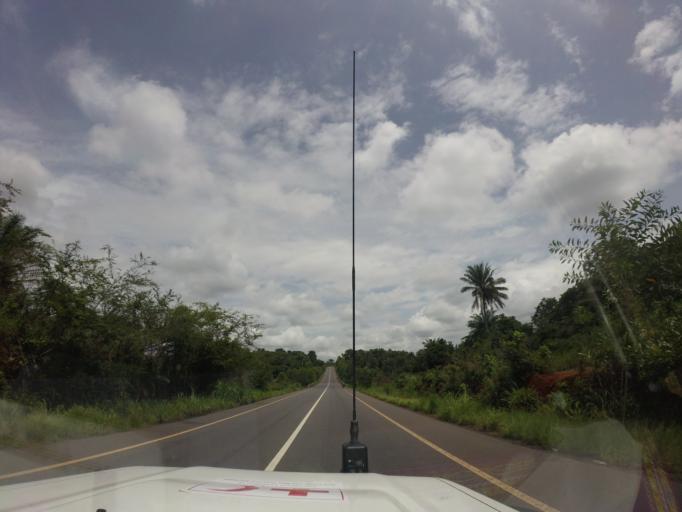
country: SL
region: Northern Province
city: Port Loko
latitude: 8.7575
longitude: -12.7720
